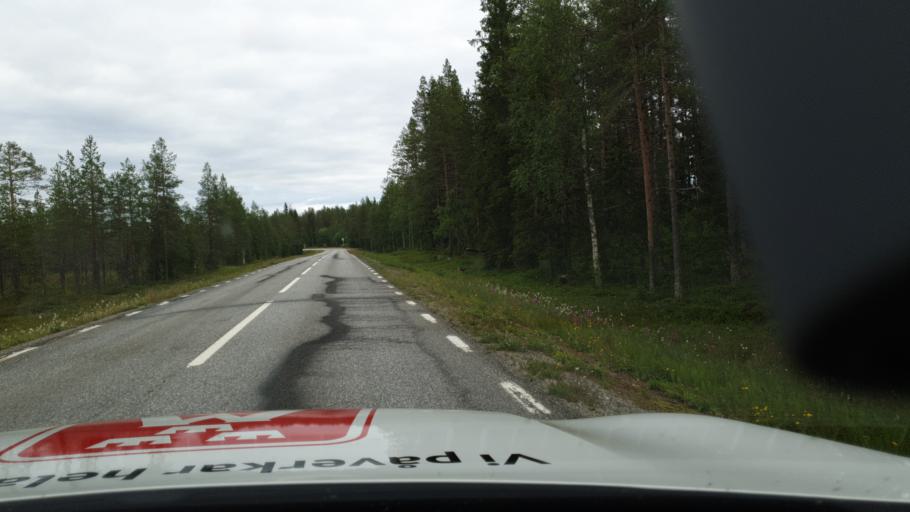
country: SE
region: Vaesterbotten
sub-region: Lycksele Kommun
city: Soderfors
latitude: 64.6164
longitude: 18.1707
